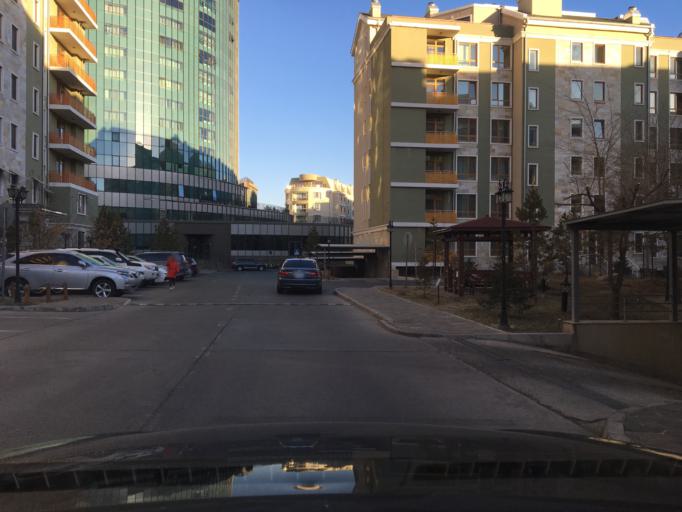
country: MN
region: Ulaanbaatar
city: Ulaanbaatar
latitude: 47.8898
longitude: 106.9312
